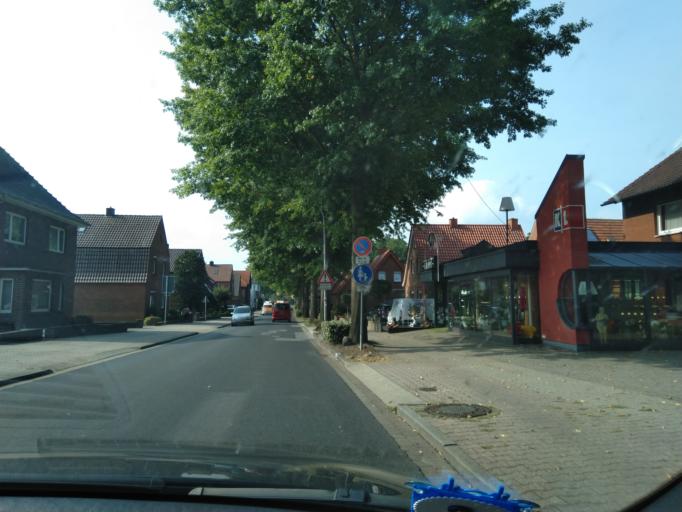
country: DE
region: Lower Saxony
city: Meppen
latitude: 52.6860
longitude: 7.2961
